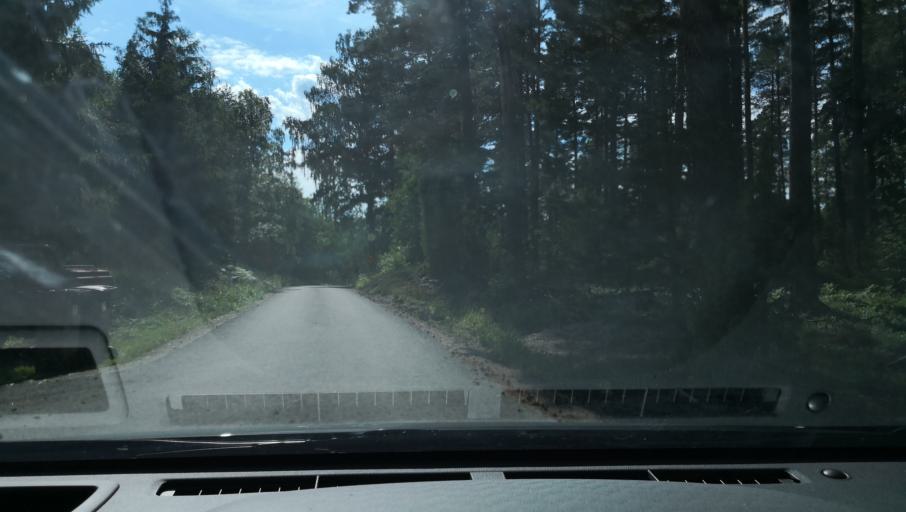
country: SE
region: Uppsala
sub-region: Enkopings Kommun
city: Orsundsbro
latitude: 59.8392
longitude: 17.2731
